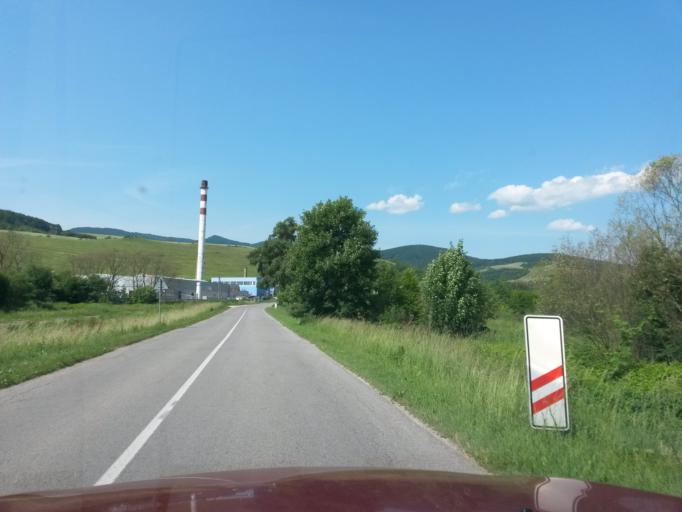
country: SK
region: Kosicky
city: Medzev
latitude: 48.6981
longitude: 20.9099
